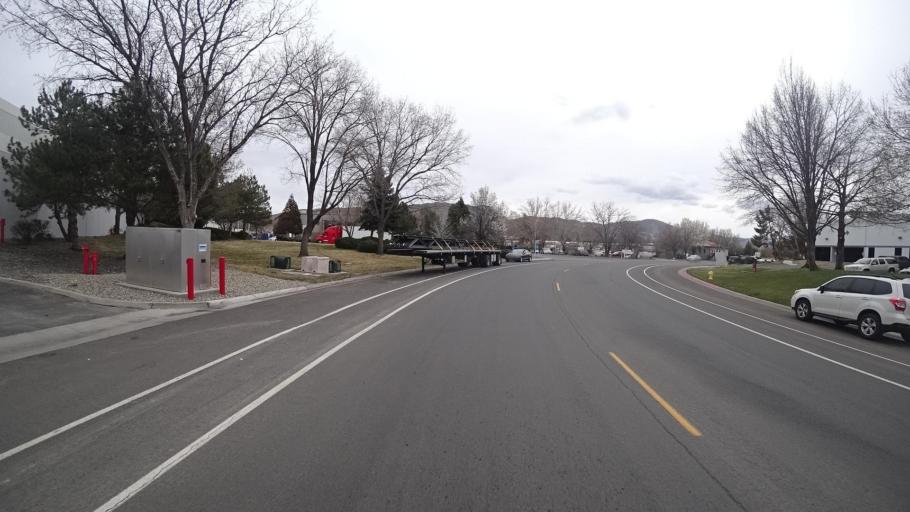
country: US
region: Nevada
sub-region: Washoe County
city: Sparks
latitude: 39.5166
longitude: -119.7348
